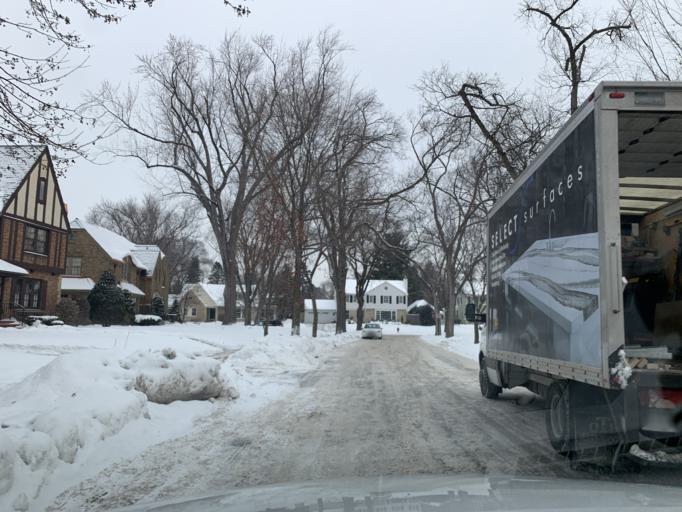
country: US
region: Minnesota
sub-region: Hennepin County
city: Edina
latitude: 44.9179
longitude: -93.3429
